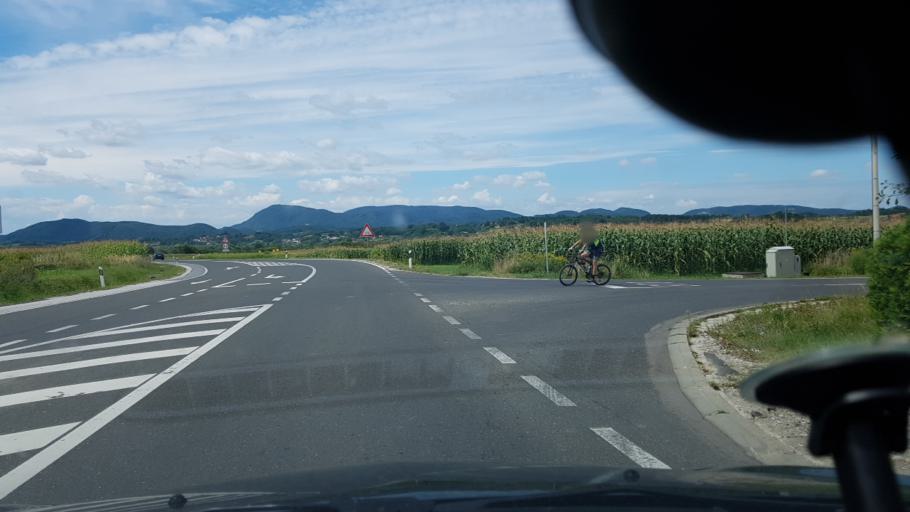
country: HR
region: Varazdinska
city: Ivanec
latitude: 46.2241
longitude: 16.0920
